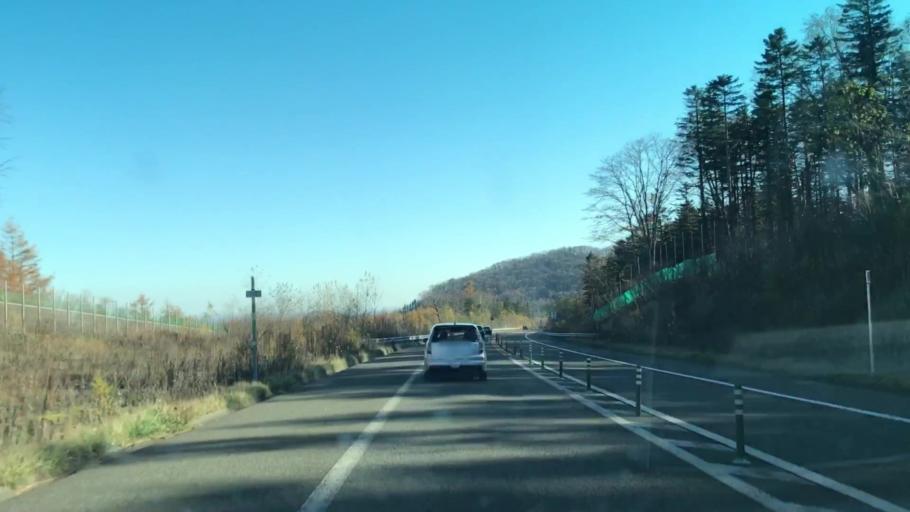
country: JP
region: Hokkaido
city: Otofuke
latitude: 43.0156
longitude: 142.8298
